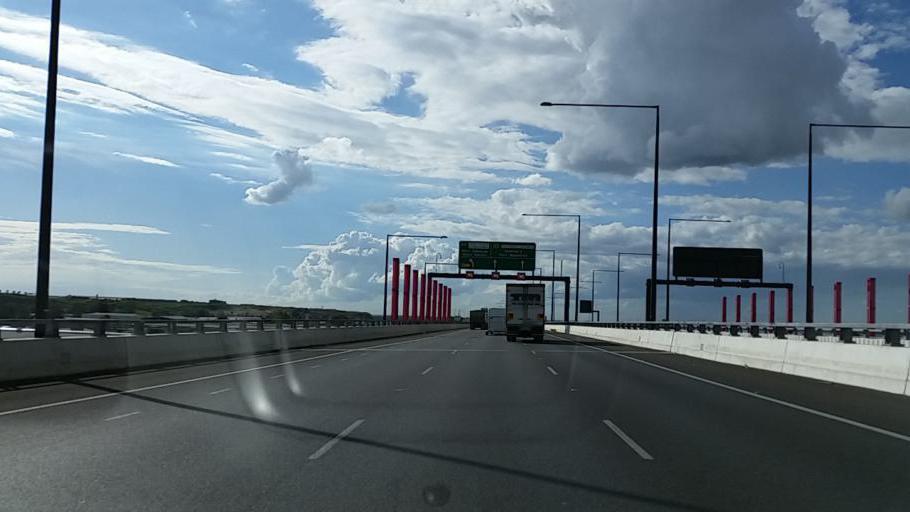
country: AU
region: South Australia
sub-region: Charles Sturt
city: Woodville North
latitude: -34.8412
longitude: 138.5639
